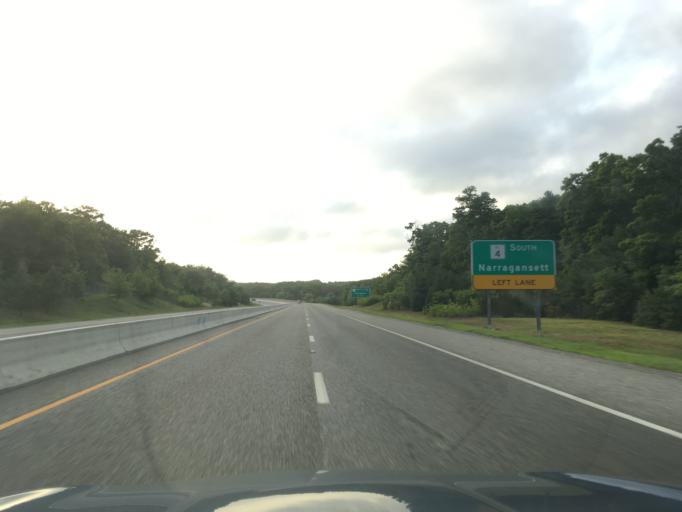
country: US
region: Rhode Island
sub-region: Kent County
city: East Greenwich
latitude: 41.6249
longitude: -71.4747
